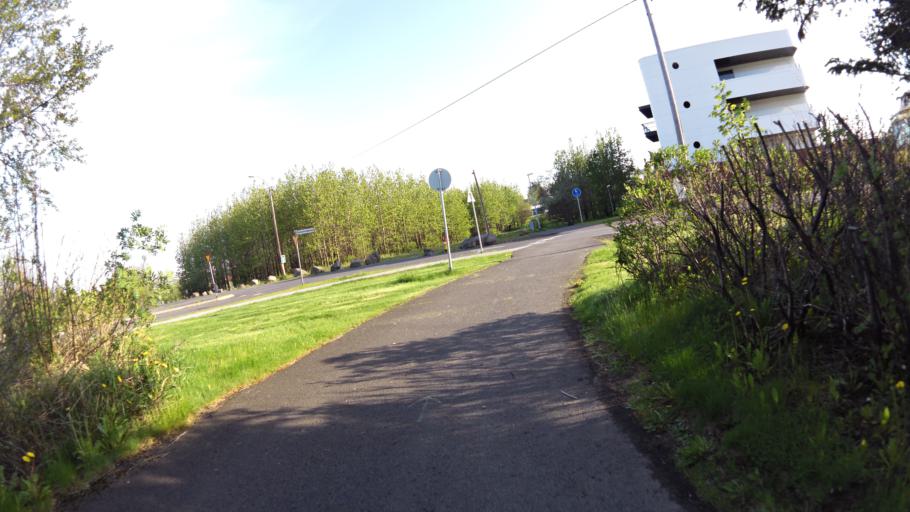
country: IS
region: Capital Region
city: Reykjavik
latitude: 64.1281
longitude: -21.8563
